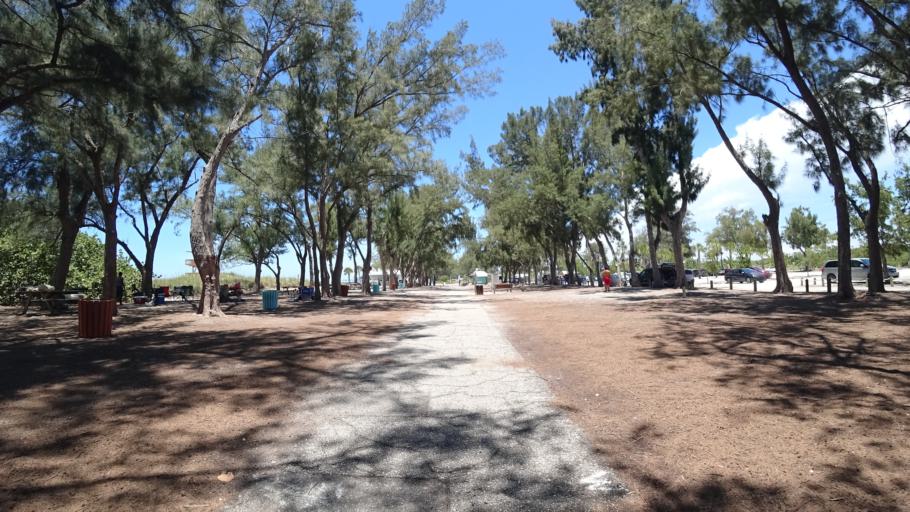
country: US
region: Florida
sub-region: Manatee County
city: Cortez
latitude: 27.4499
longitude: -82.6920
